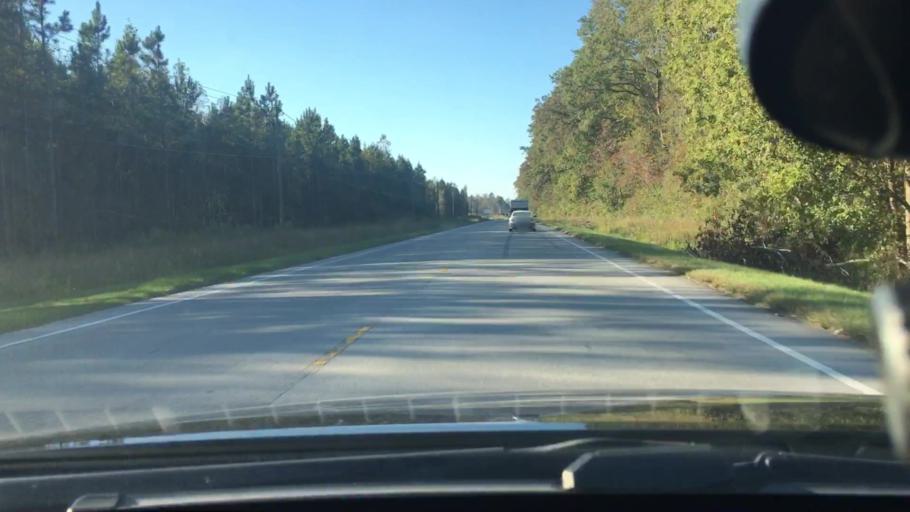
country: US
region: North Carolina
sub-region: Craven County
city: Vanceboro
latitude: 35.2437
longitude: -77.0823
